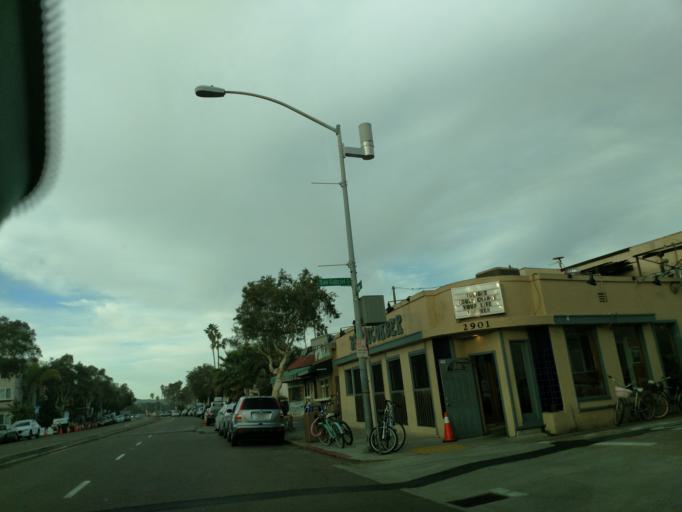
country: US
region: California
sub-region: San Diego County
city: La Jolla
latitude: 32.7655
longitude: -117.2513
